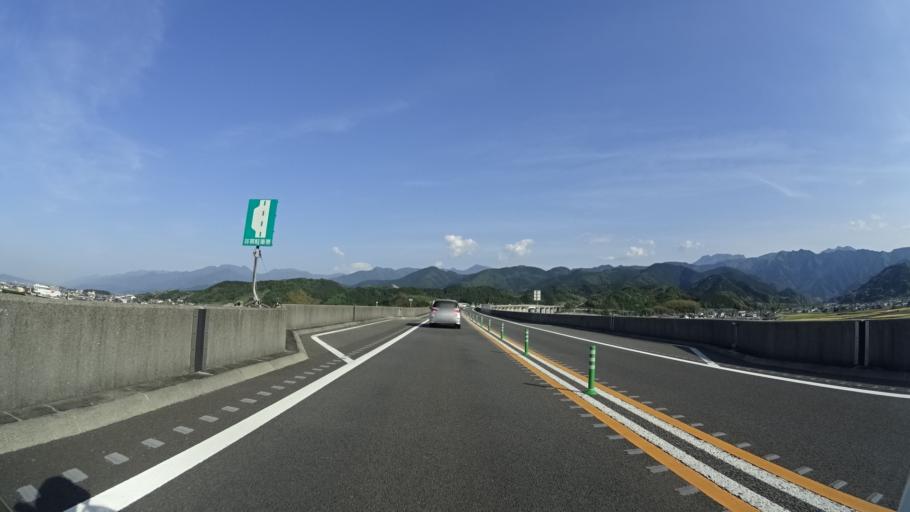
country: JP
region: Ehime
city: Saijo
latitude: 33.8943
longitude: 133.0818
